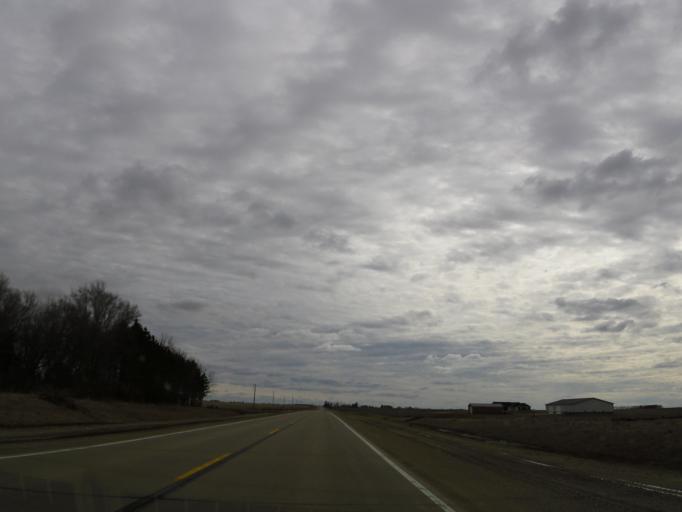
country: US
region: Iowa
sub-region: Howard County
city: Cresco
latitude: 43.4224
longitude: -92.2986
